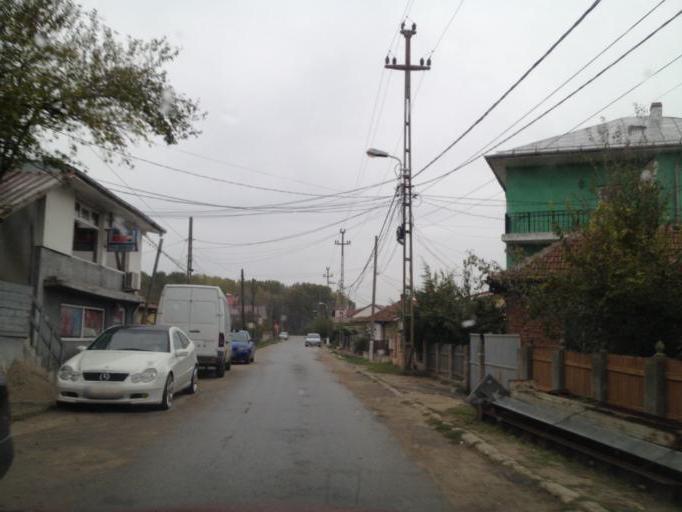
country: RO
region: Dolj
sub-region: Municipiul Craiova
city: Mofleni
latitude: 44.2988
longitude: 23.7577
